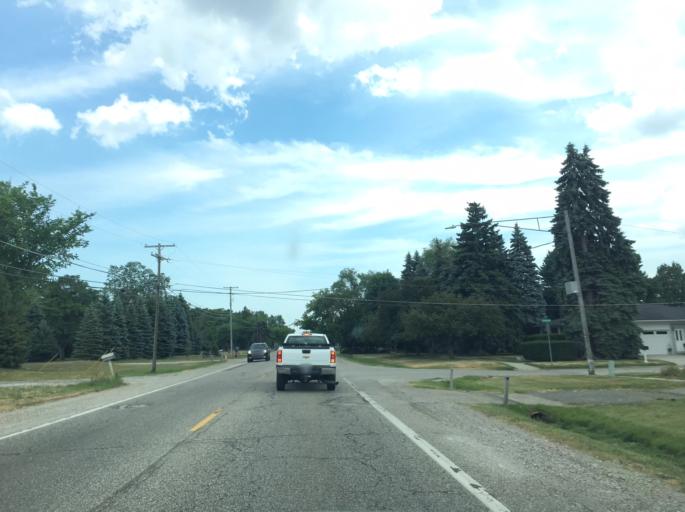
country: US
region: Michigan
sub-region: Macomb County
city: Sterling Heights
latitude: 42.5998
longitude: -83.0206
